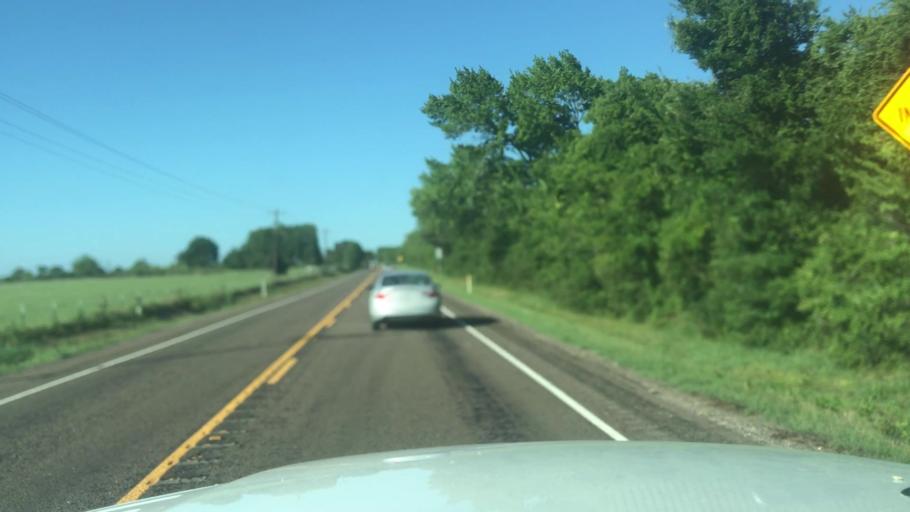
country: US
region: Texas
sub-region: Grimes County
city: Anderson
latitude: 30.6348
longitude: -95.8654
